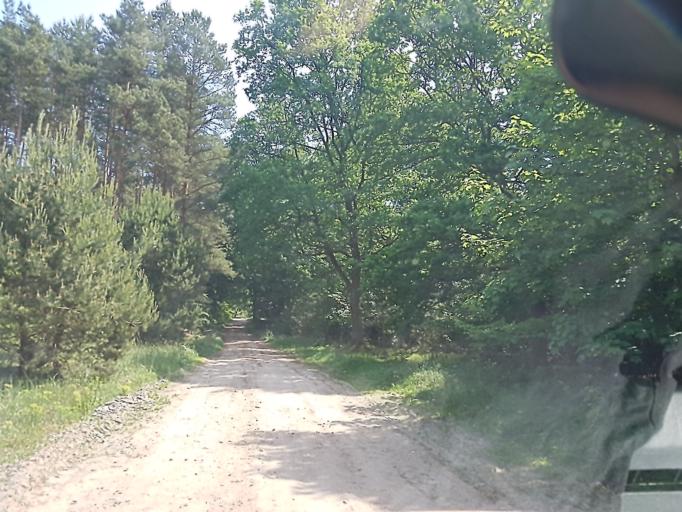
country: DE
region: Brandenburg
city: Gorzke
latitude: 52.0927
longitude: 12.3325
